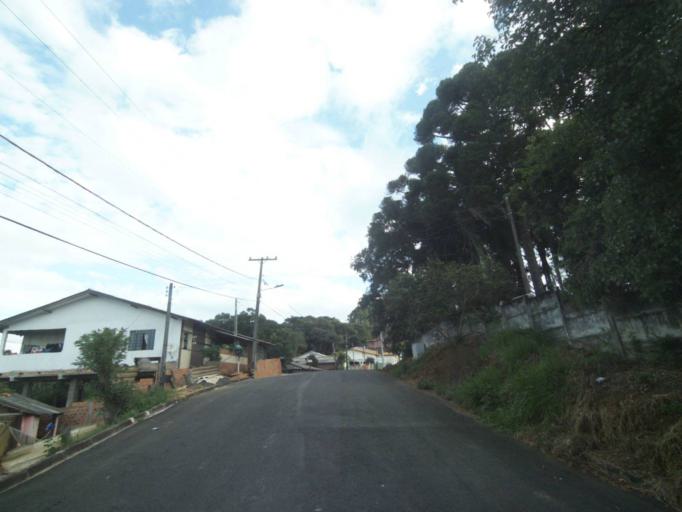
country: BR
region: Parana
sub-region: Telemaco Borba
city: Telemaco Borba
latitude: -24.3275
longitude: -50.6080
